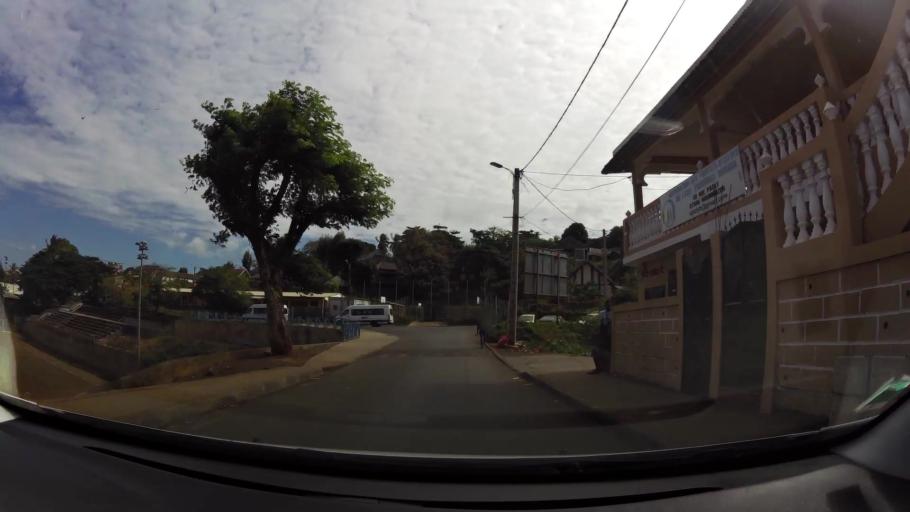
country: YT
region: Mamoudzou
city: Mamoudzou
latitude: -12.7809
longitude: 45.2279
